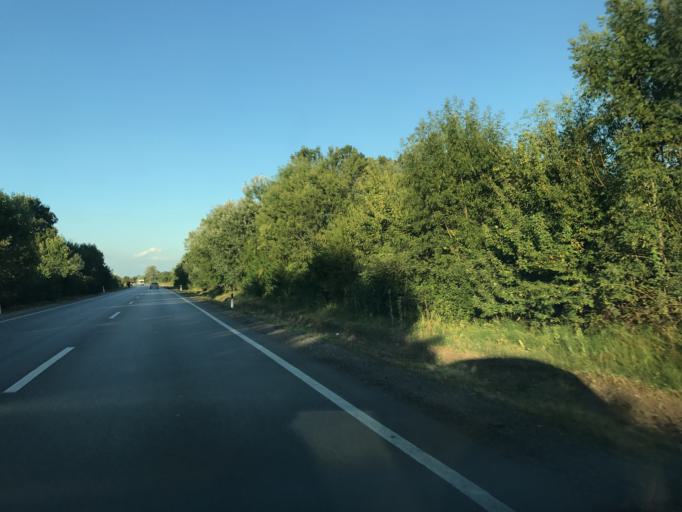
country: RS
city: Lugavcina
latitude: 44.5942
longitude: 21.0337
